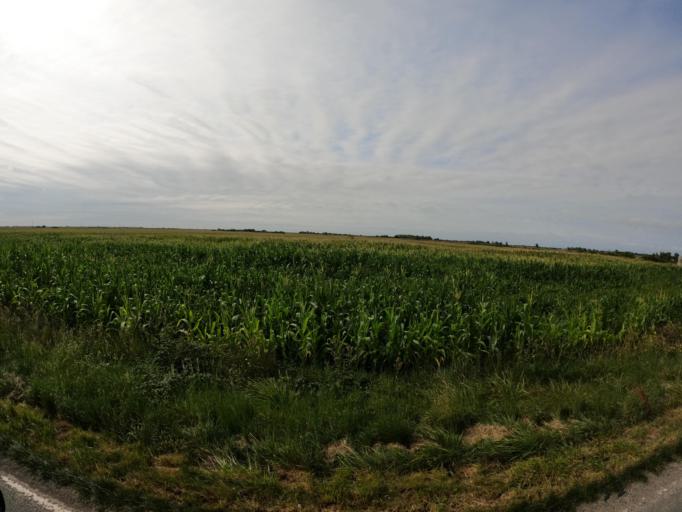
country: FR
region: Pays de la Loire
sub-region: Departement de la Vendee
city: Triaize
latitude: 46.3681
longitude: -1.2222
